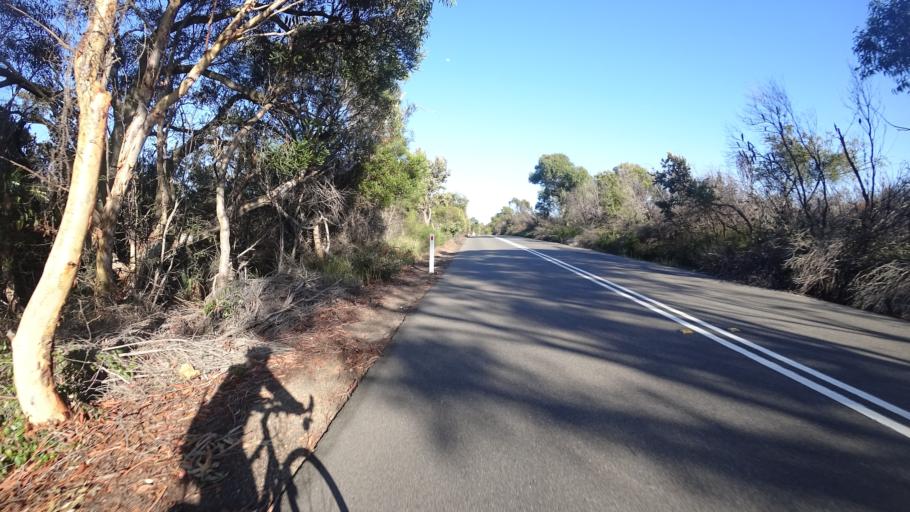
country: AU
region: New South Wales
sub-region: Pittwater
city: Ingleside
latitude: -33.6692
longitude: 151.2327
